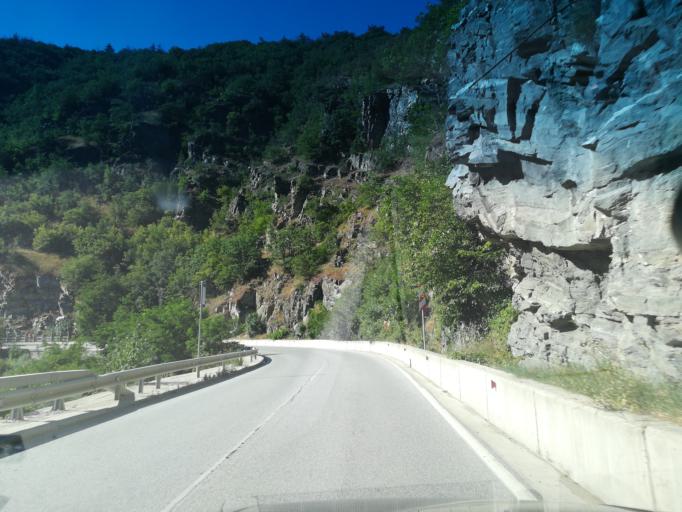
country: BG
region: Plovdiv
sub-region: Obshtina Luki
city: Luki
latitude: 41.9061
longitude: 24.7637
